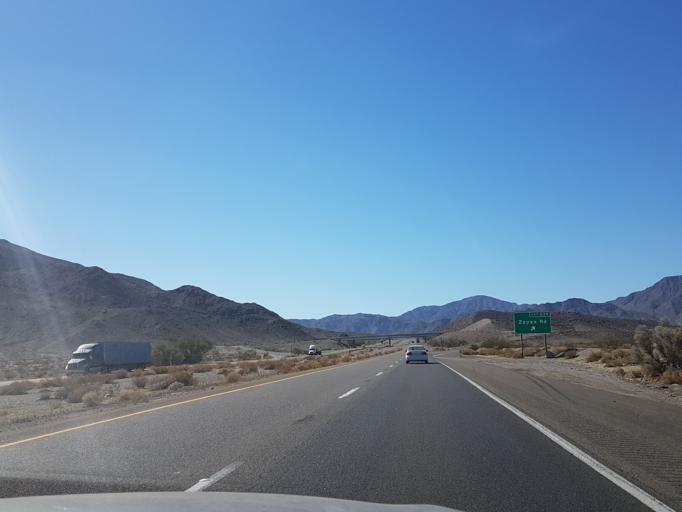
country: US
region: California
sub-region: San Bernardino County
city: Fort Irwin
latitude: 35.1965
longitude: -116.1353
